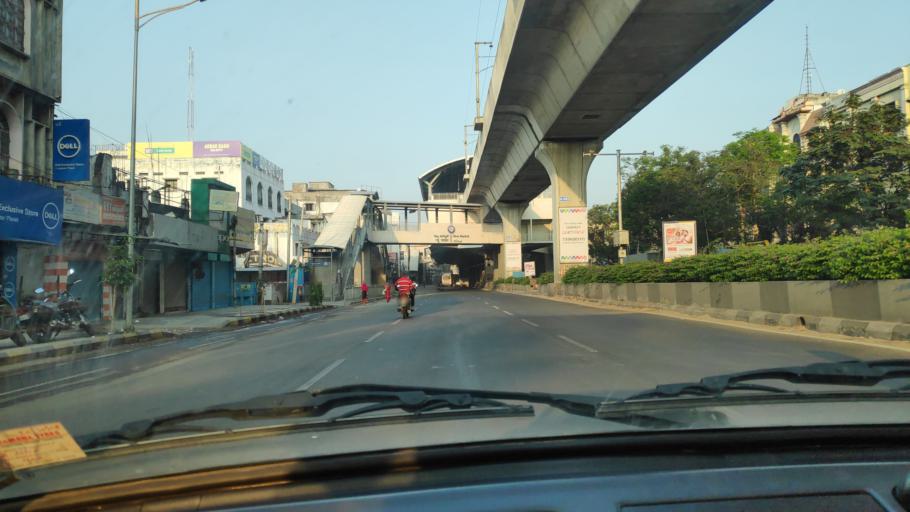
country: IN
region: Telangana
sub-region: Rangareddi
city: Gaddi Annaram
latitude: 17.3732
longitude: 78.5047
